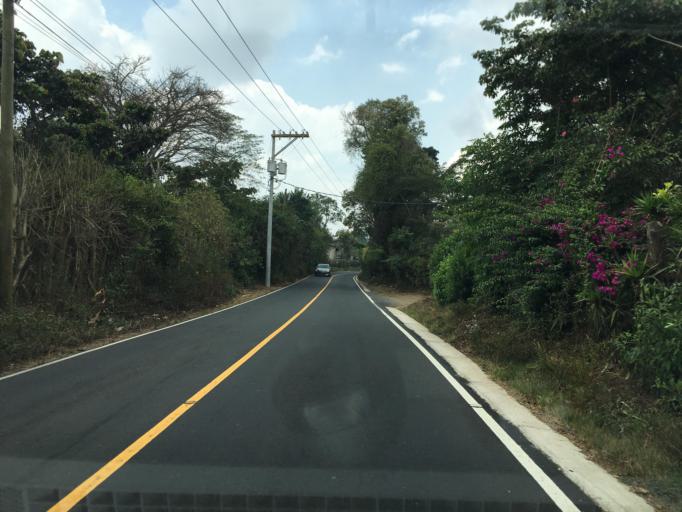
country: GT
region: Guatemala
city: Villa Canales
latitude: 14.4226
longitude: -90.5250
